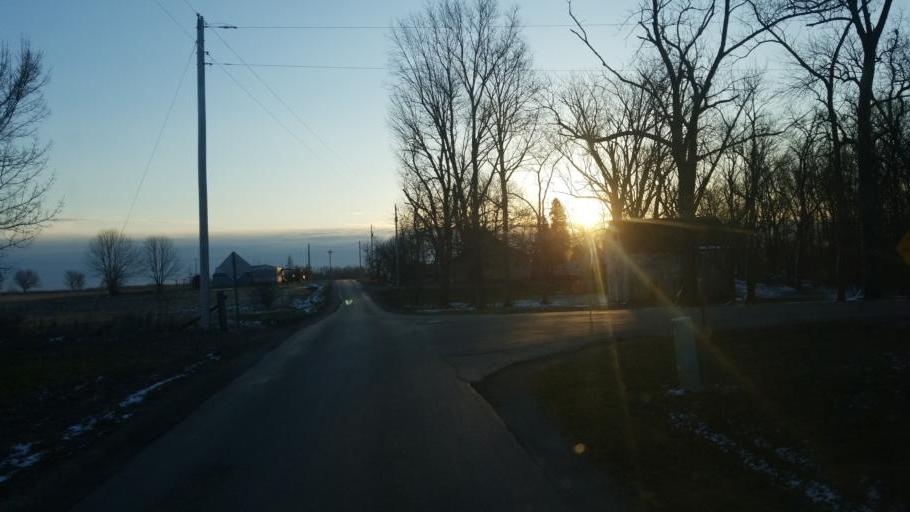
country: US
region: Ohio
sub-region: Highland County
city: Leesburg
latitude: 39.2858
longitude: -83.5043
